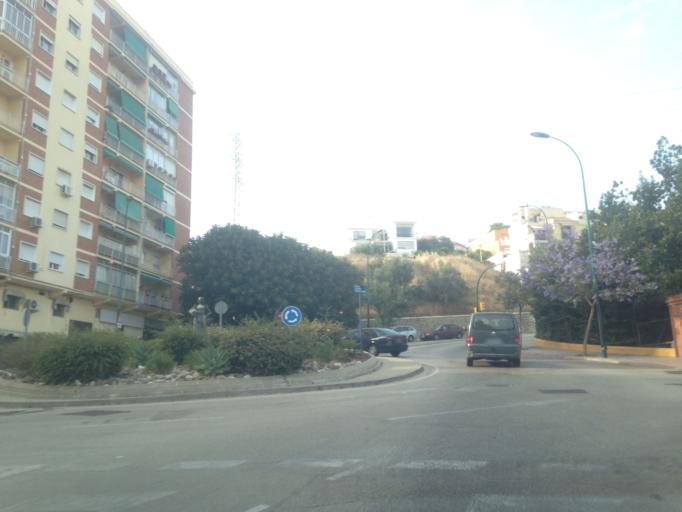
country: ES
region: Andalusia
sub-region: Provincia de Malaga
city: Malaga
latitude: 36.7359
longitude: -4.4159
